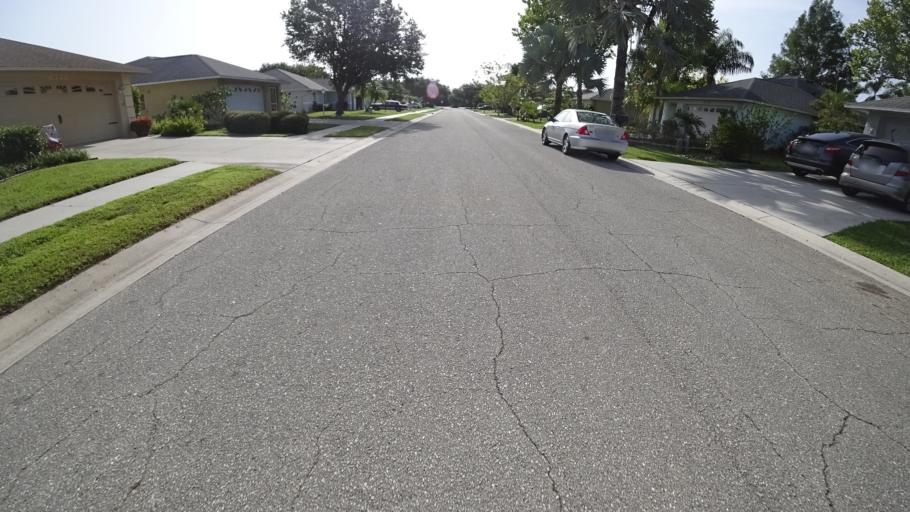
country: US
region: Florida
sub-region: Sarasota County
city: Desoto Lakes
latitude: 27.4234
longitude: -82.4733
